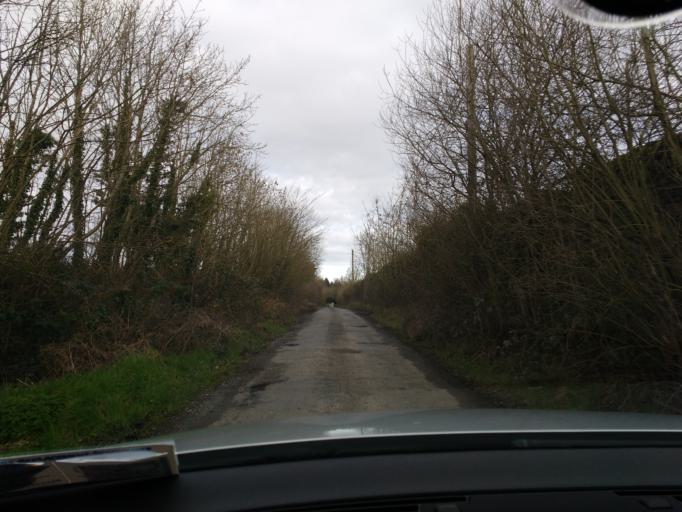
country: IE
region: Leinster
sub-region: Laois
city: Rathdowney
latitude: 52.6644
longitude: -7.5670
